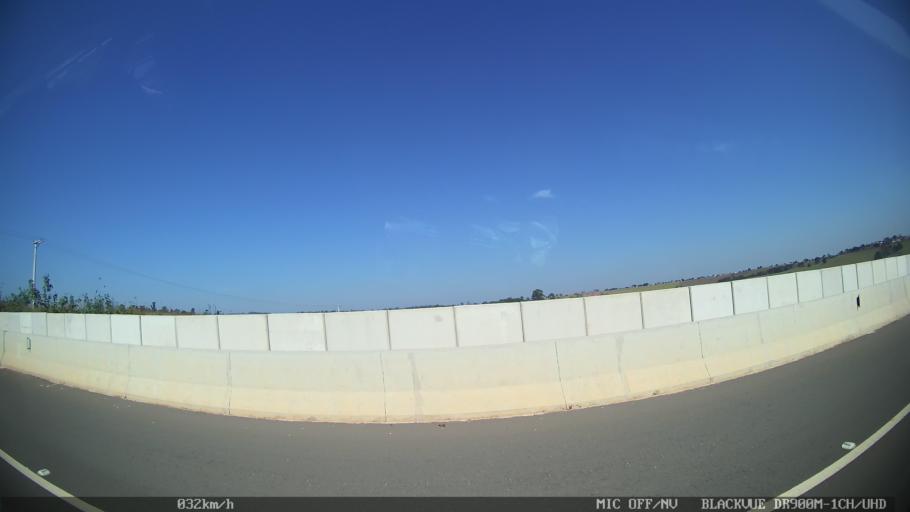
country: BR
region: Sao Paulo
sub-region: Valinhos
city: Valinhos
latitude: -23.0258
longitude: -47.0875
